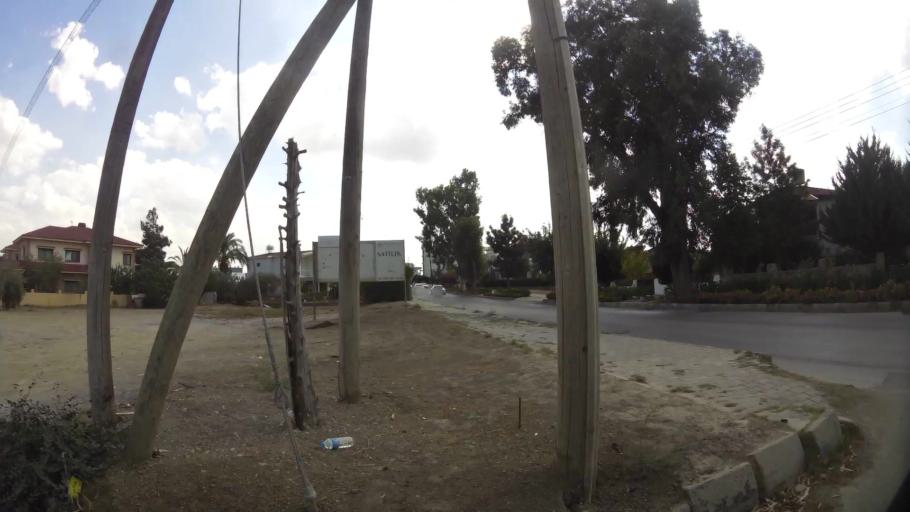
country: CY
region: Lefkosia
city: Nicosia
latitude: 35.2243
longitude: 33.2996
